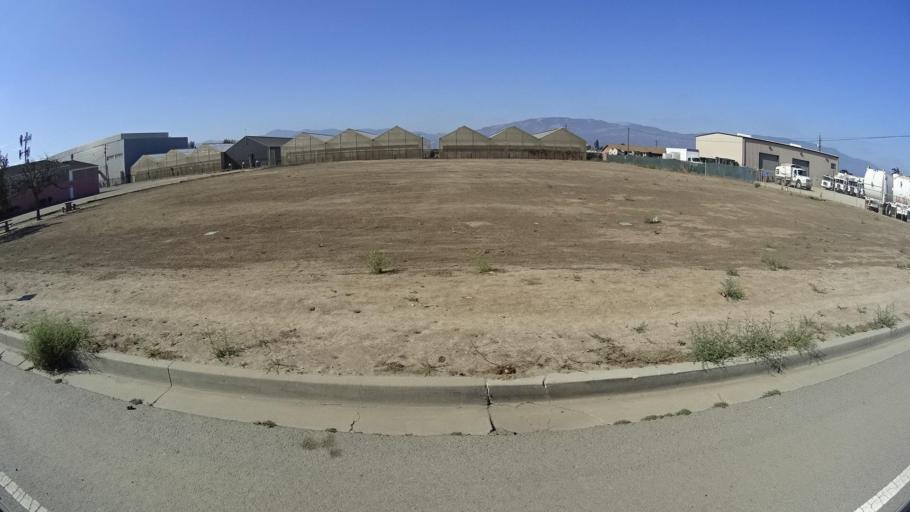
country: US
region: California
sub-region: Monterey County
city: Greenfield
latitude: 36.3312
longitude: -121.2520
